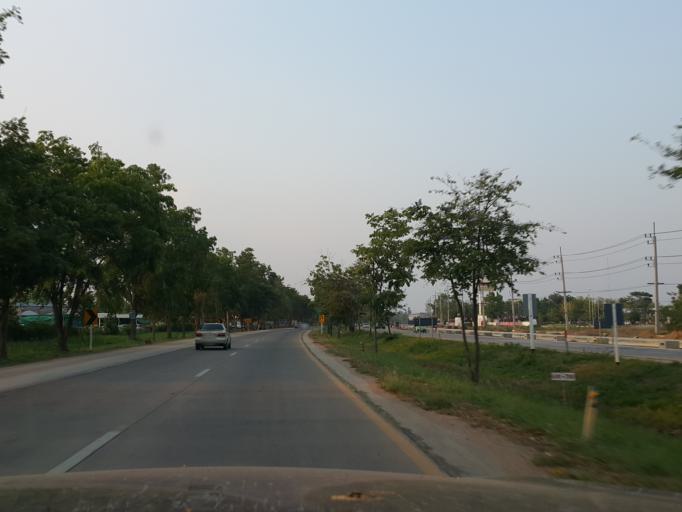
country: TH
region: Lampang
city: Ko Kha
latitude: 18.1970
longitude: 99.4069
